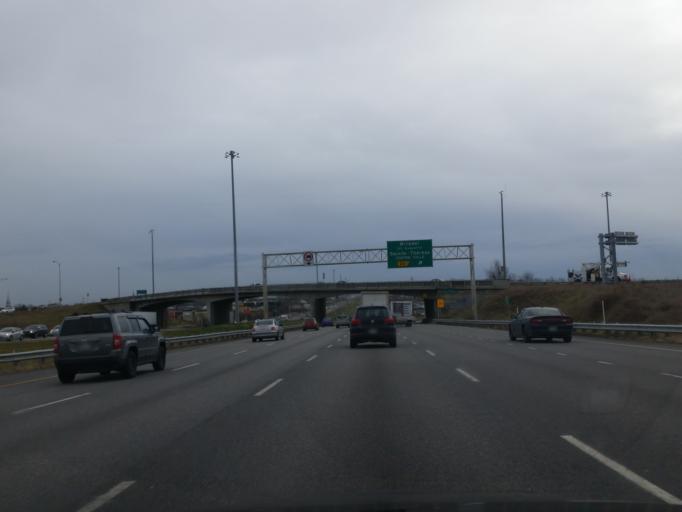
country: CA
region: Quebec
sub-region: Laurentides
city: Blainville
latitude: 45.6462
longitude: -73.8683
